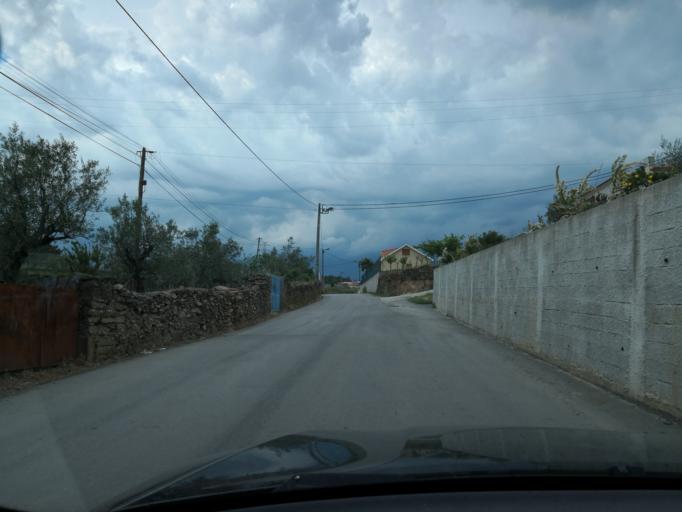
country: PT
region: Vila Real
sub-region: Sabrosa
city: Vilela
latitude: 41.2144
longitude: -7.6691
